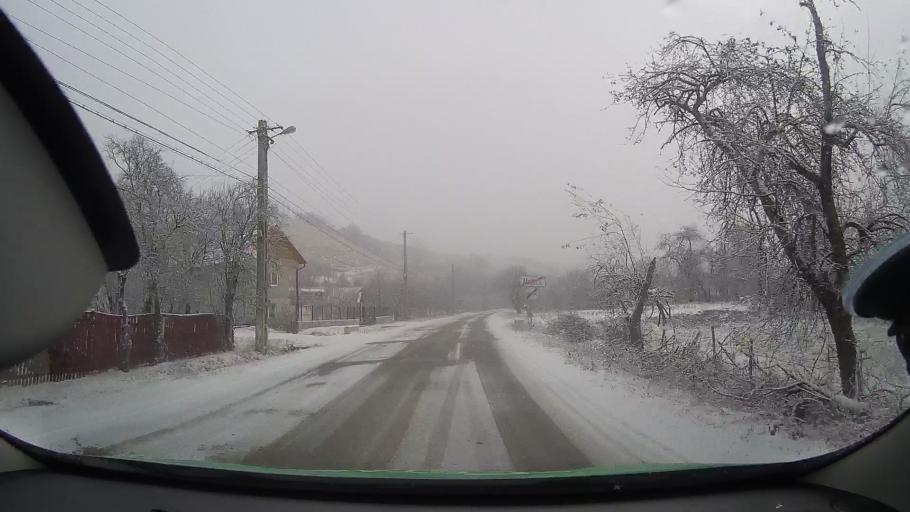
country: RO
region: Alba
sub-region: Comuna Livezile
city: Livezile
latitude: 46.3414
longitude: 23.6643
